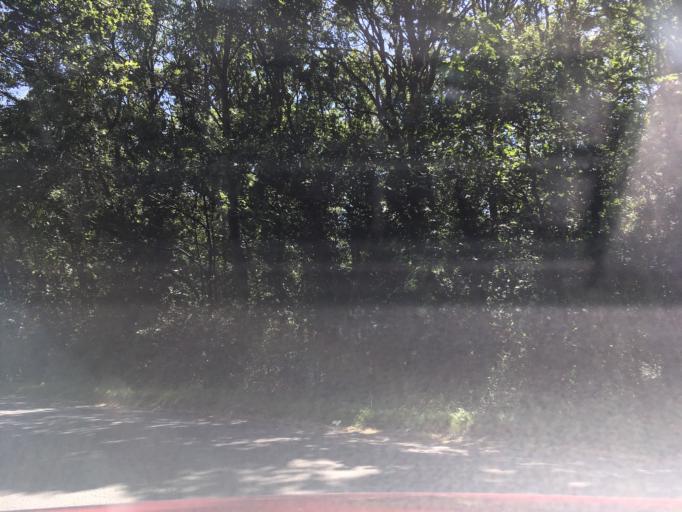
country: GB
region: England
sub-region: Northamptonshire
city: Deanshanger
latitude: 52.0060
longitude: -0.8905
